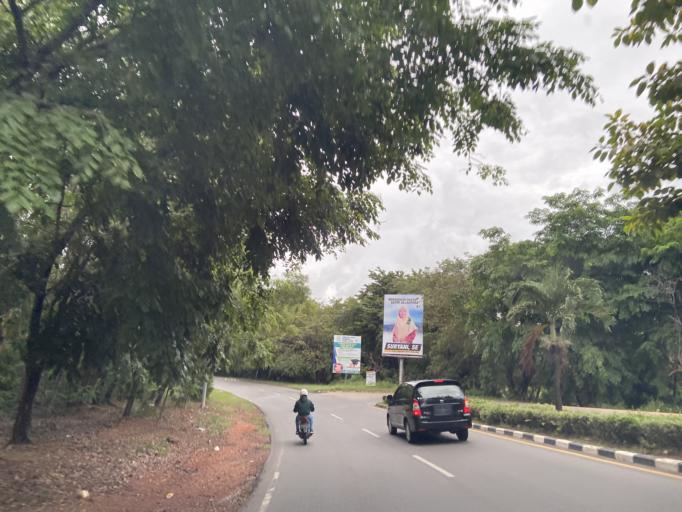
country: SG
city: Singapore
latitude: 1.1221
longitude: 104.0154
